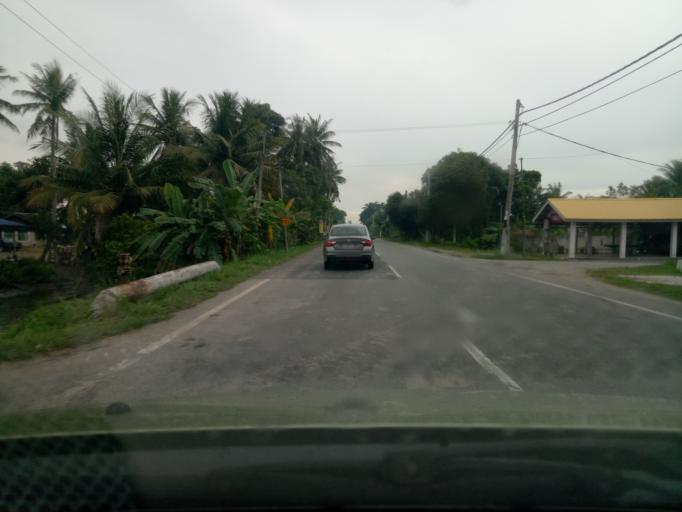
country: MY
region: Kedah
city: Alor Setar
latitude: 5.9728
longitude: 100.4104
